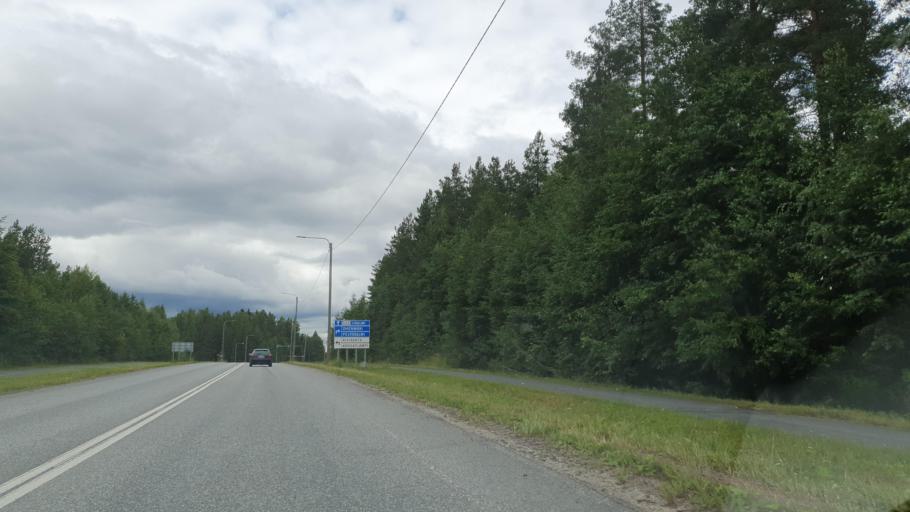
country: FI
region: Northern Savo
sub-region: Ylae-Savo
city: Iisalmi
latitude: 63.5202
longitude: 27.2398
